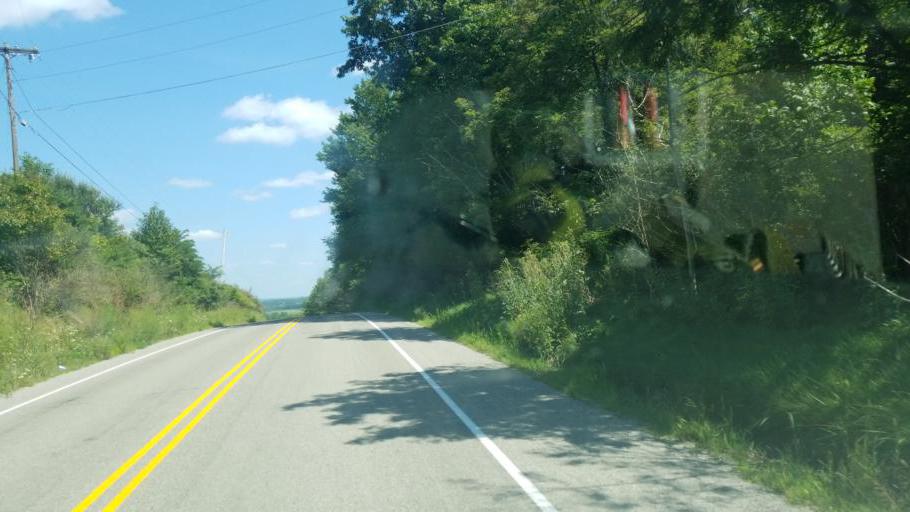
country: US
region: Pennsylvania
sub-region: Clarion County
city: Knox
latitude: 41.1093
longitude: -79.6098
